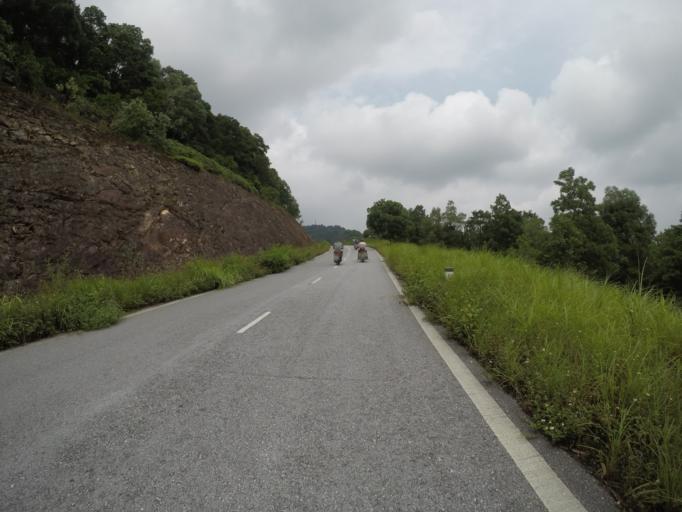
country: VN
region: Ha Noi
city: Soc Son
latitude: 21.2800
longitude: 105.8256
